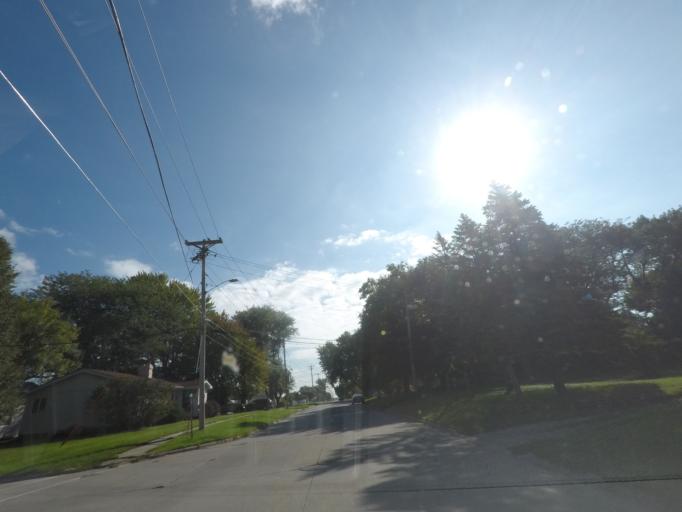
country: US
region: Iowa
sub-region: Story County
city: Nevada
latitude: 42.0191
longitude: -93.4426
